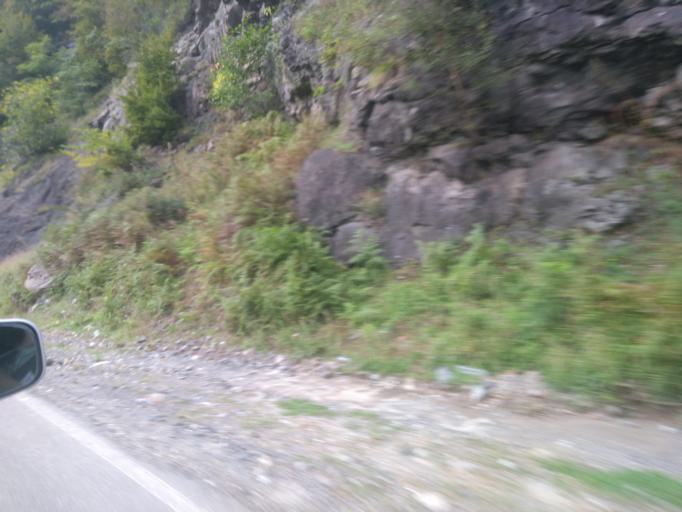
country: GE
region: Ajaria
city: Khelvachauri
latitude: 41.5514
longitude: 41.7015
